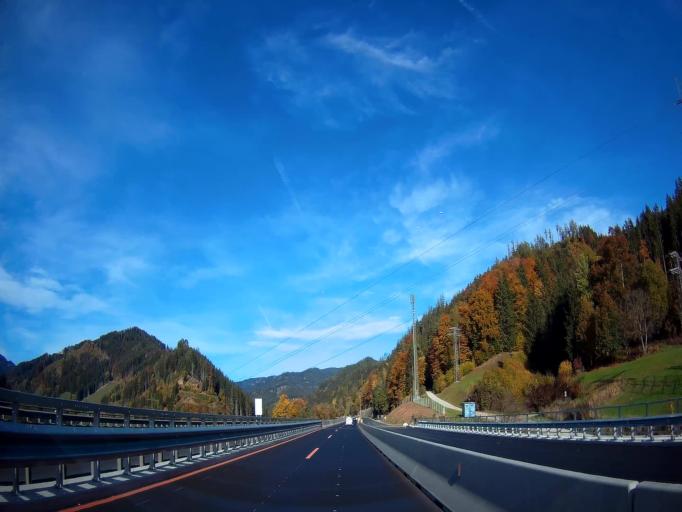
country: AT
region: Styria
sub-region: Politischer Bezirk Graz-Umgebung
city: Ubelbach
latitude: 47.2312
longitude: 15.2153
